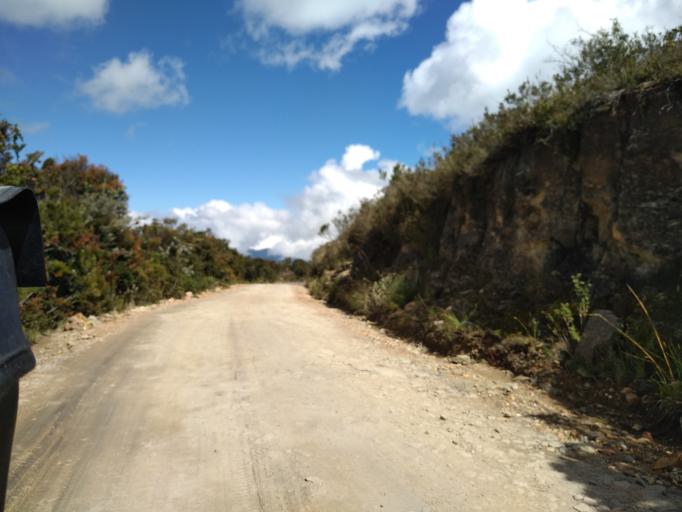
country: CO
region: Boyaca
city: Duitama
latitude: 5.9344
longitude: -73.0950
